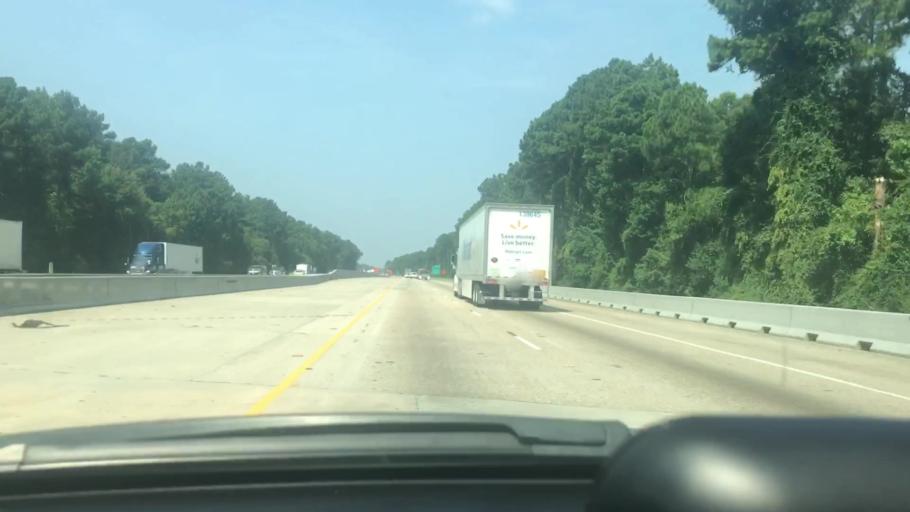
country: US
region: Louisiana
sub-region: Livingston Parish
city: Livingston
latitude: 30.4741
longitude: -90.7811
